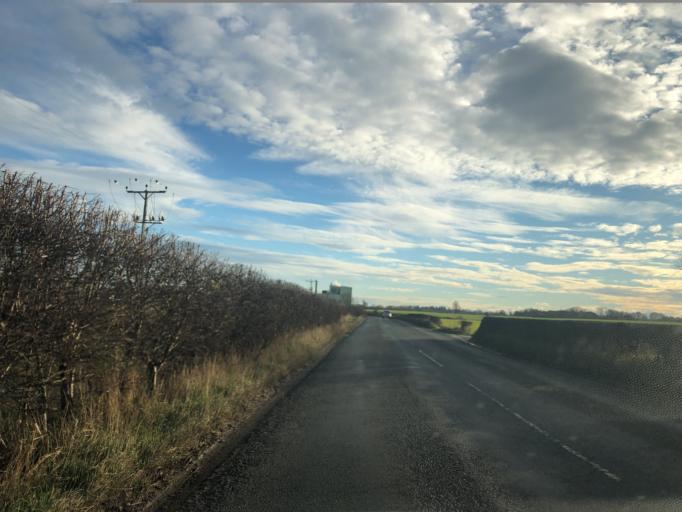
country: GB
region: England
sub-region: North Yorkshire
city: Thirsk
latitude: 54.1749
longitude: -1.3681
